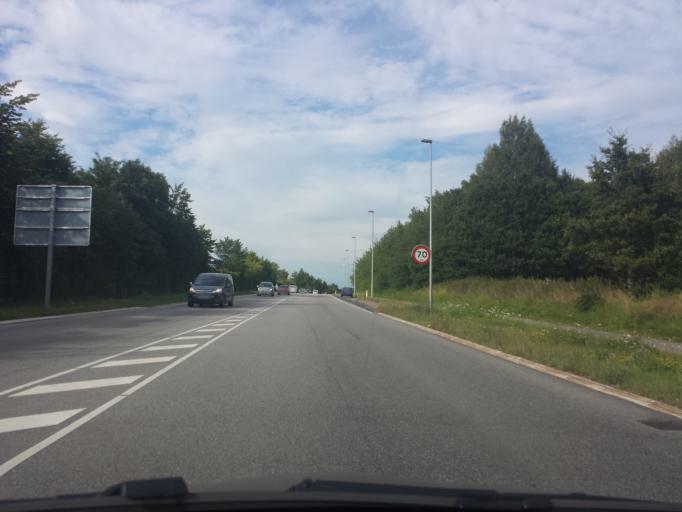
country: DK
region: Capital Region
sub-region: Ballerup Kommune
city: Ballerup
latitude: 55.7351
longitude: 12.3772
